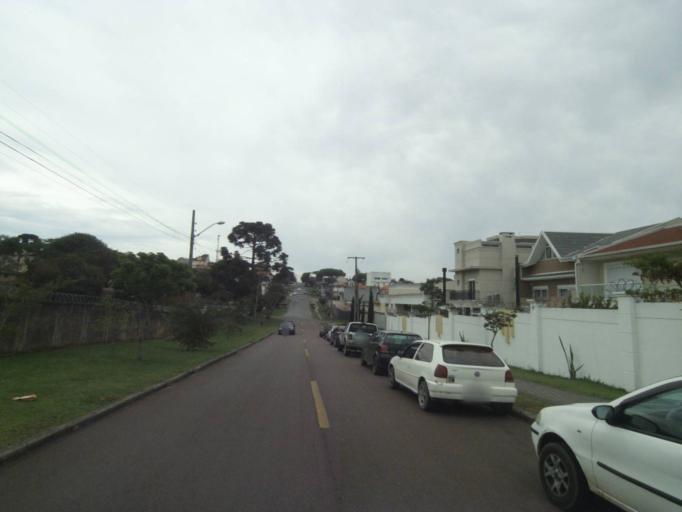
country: BR
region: Parana
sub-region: Pinhais
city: Pinhais
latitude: -25.4114
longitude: -49.2107
